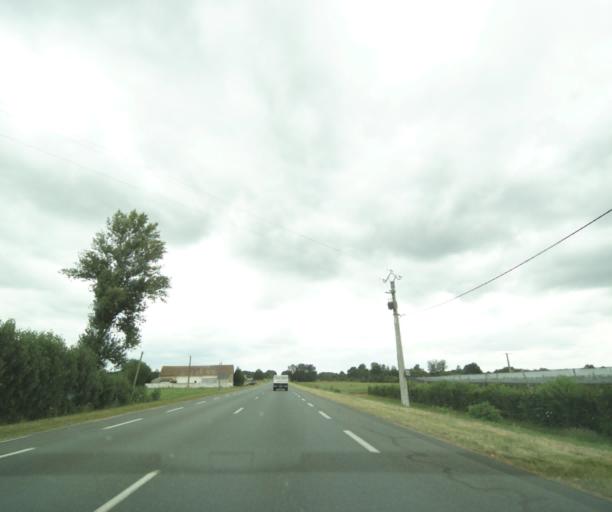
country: FR
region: Pays de la Loire
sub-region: Departement de Maine-et-Loire
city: Durtal
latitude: 47.6466
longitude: -0.2705
